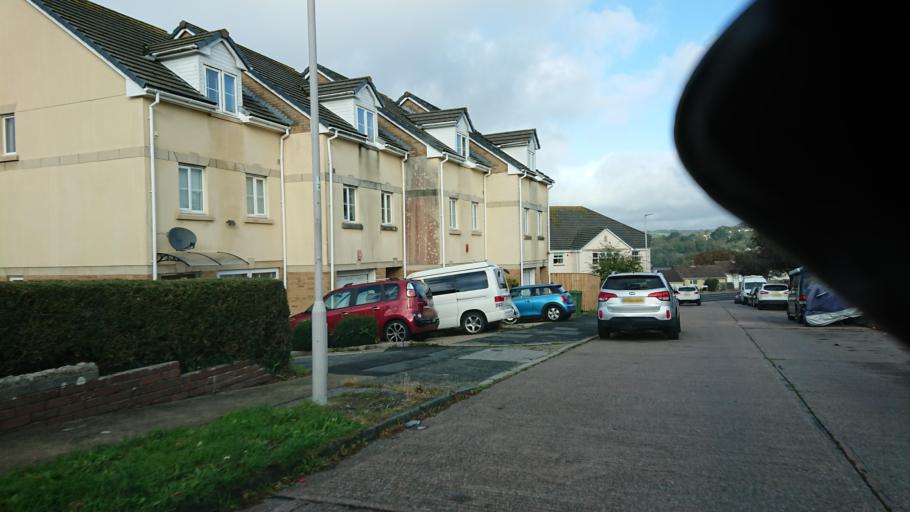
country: GB
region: England
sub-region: Cornwall
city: Saltash
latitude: 50.4209
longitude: -4.1774
